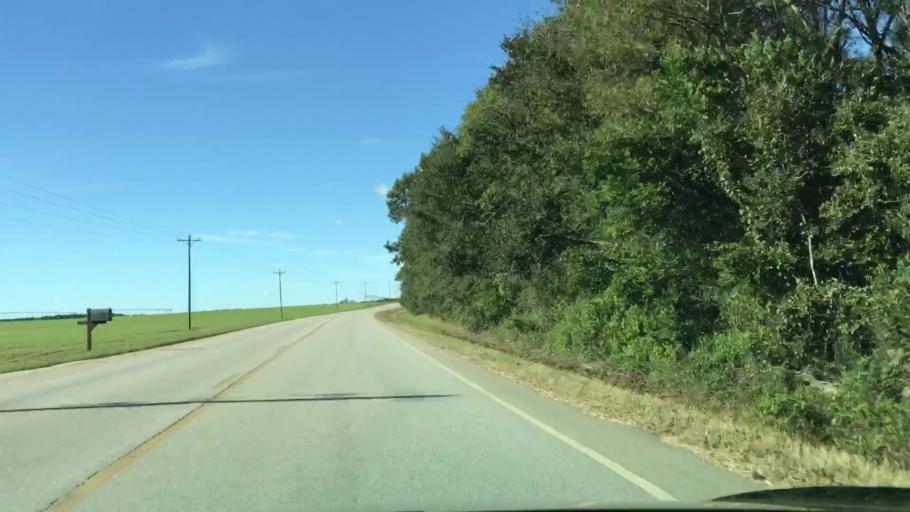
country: US
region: Georgia
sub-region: Jefferson County
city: Louisville
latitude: 33.0744
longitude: -82.4100
